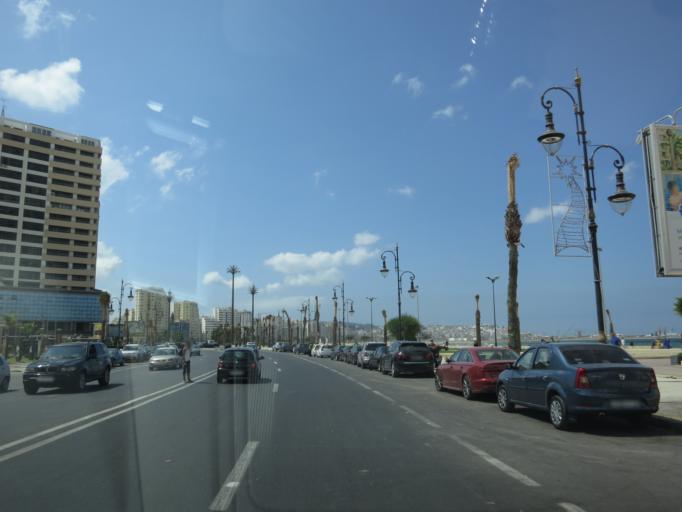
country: MA
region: Tanger-Tetouan
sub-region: Tanger-Assilah
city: Tangier
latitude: 35.7754
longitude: -5.7876
